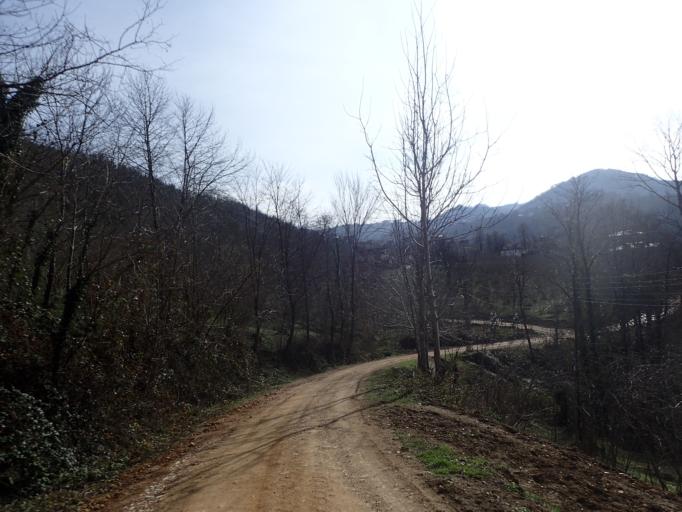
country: TR
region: Ordu
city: Camas
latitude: 40.9399
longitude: 37.5144
